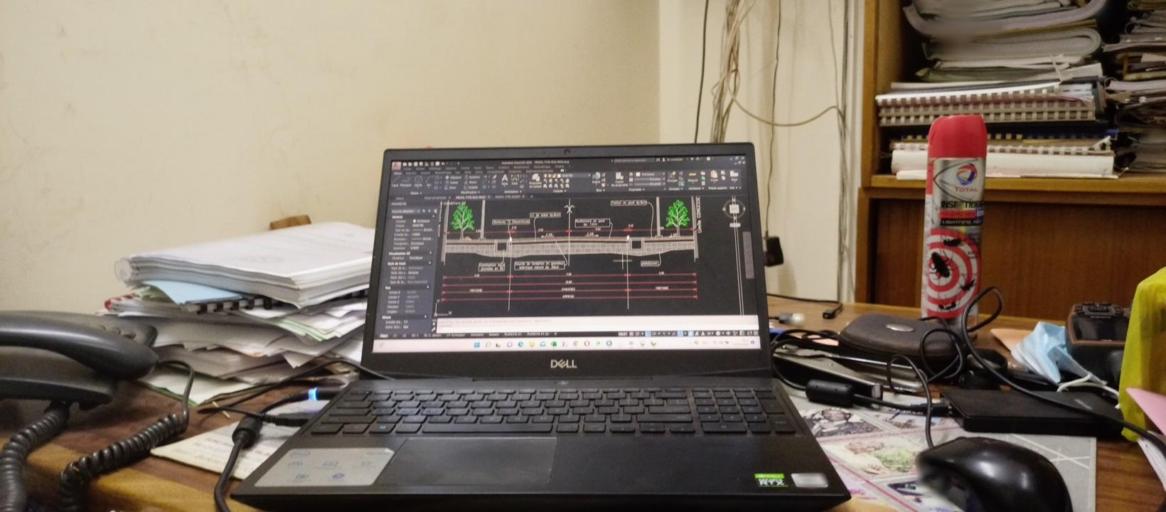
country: BF
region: Centre
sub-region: Kadiogo Province
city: Ouagadougou
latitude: 12.3346
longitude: -1.5469
